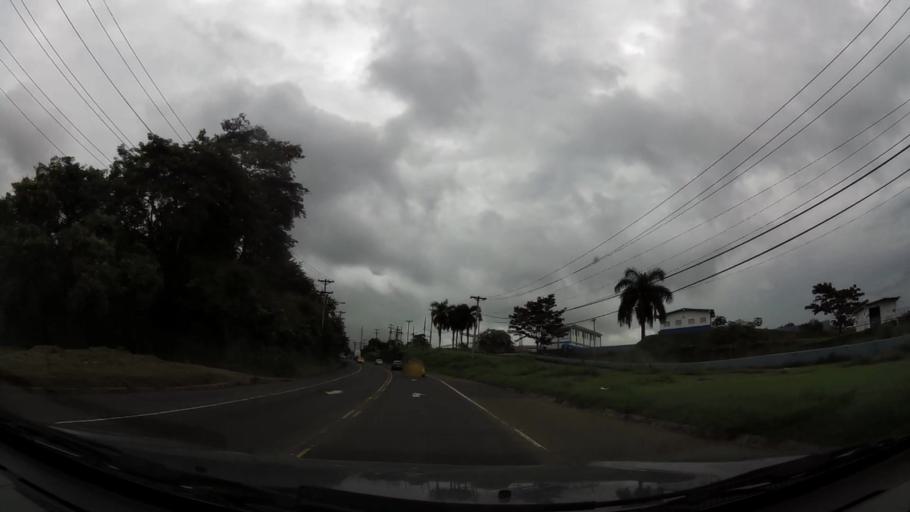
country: PA
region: Panama
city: Chilibre
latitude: 9.1918
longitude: -79.6180
